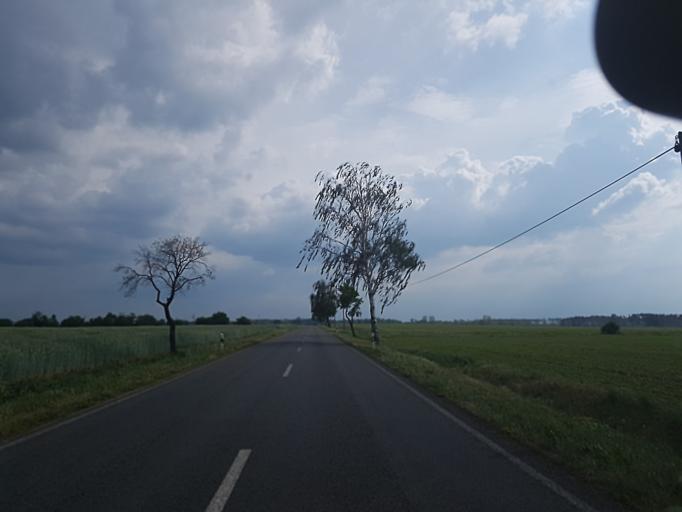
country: DE
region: Saxony-Anhalt
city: Rodleben
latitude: 52.0018
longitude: 12.2330
